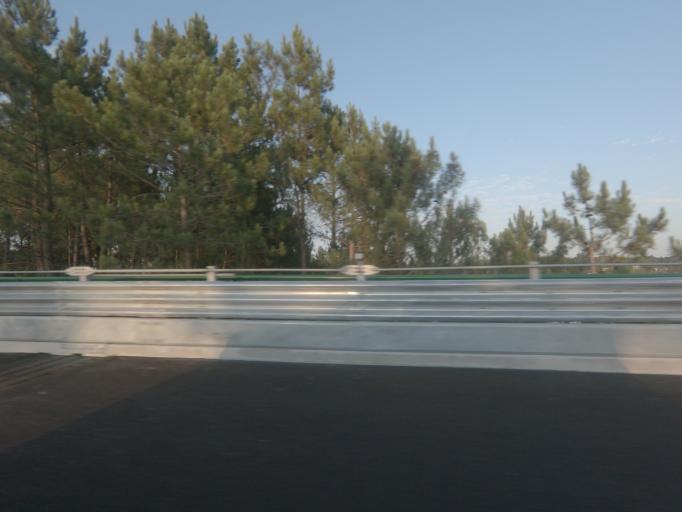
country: PT
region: Leiria
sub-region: Leiria
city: Caranguejeira
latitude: 39.8082
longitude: -8.7221
